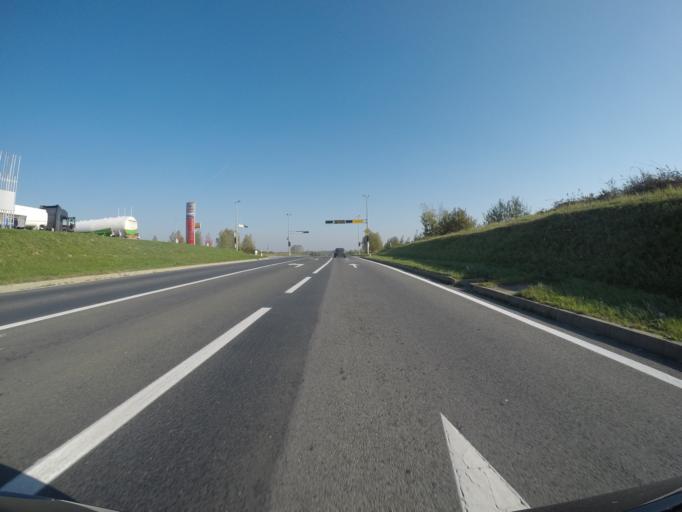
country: HR
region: Bjelovarsko-Bilogorska
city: Bjelovar
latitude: 45.9287
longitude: 16.8387
